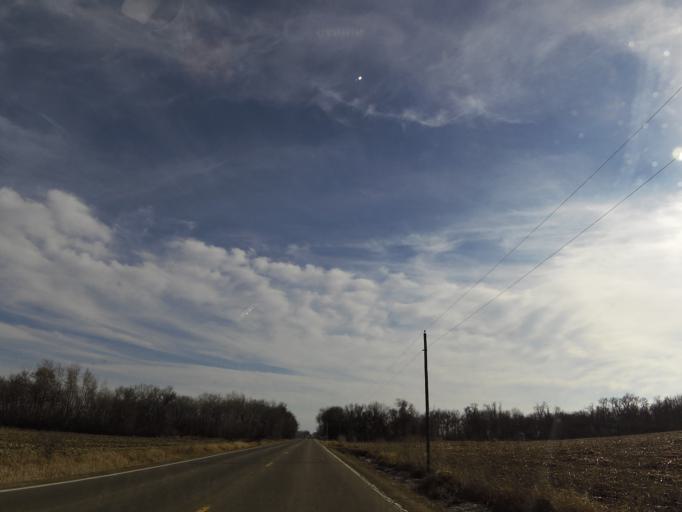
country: US
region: Minnesota
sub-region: Rice County
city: Northfield
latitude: 44.5196
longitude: -93.2006
